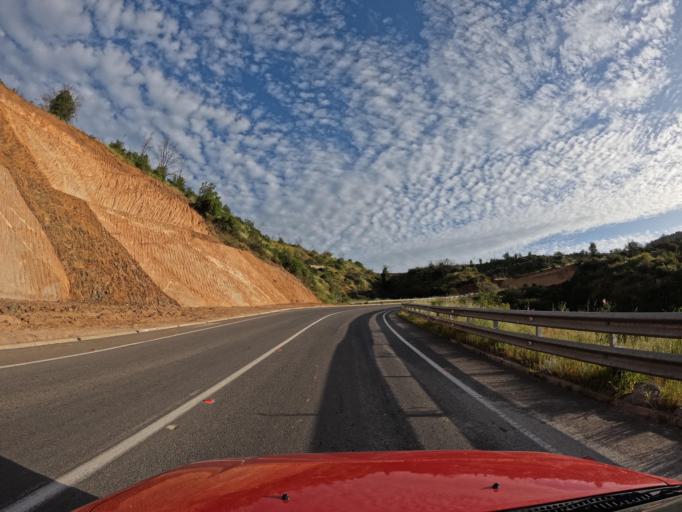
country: CL
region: Valparaiso
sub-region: San Antonio Province
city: San Antonio
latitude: -34.0410
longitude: -71.5926
